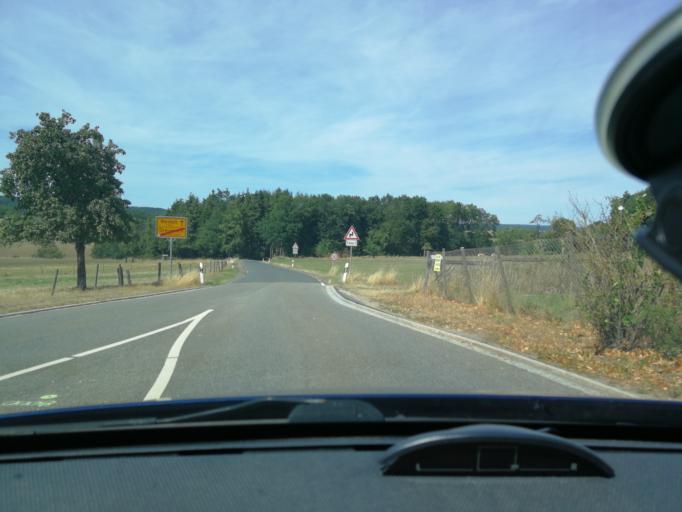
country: DE
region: Rheinland-Pfalz
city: Niersbach
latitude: 49.9320
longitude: 6.7533
